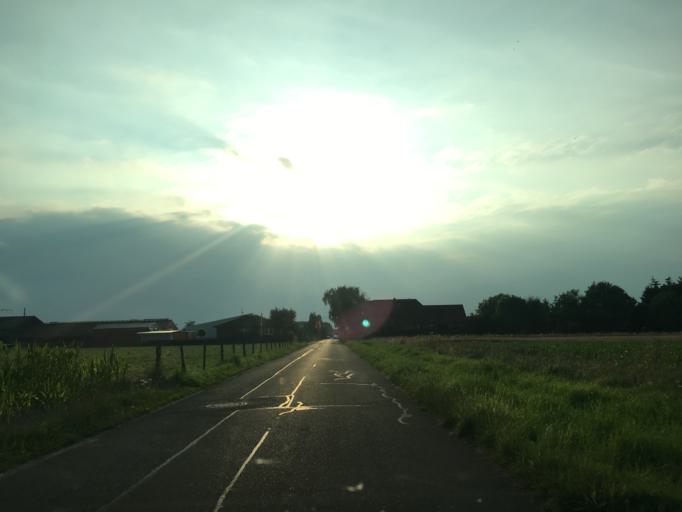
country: DE
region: North Rhine-Westphalia
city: Huckelhoven
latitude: 51.0690
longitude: 6.2439
